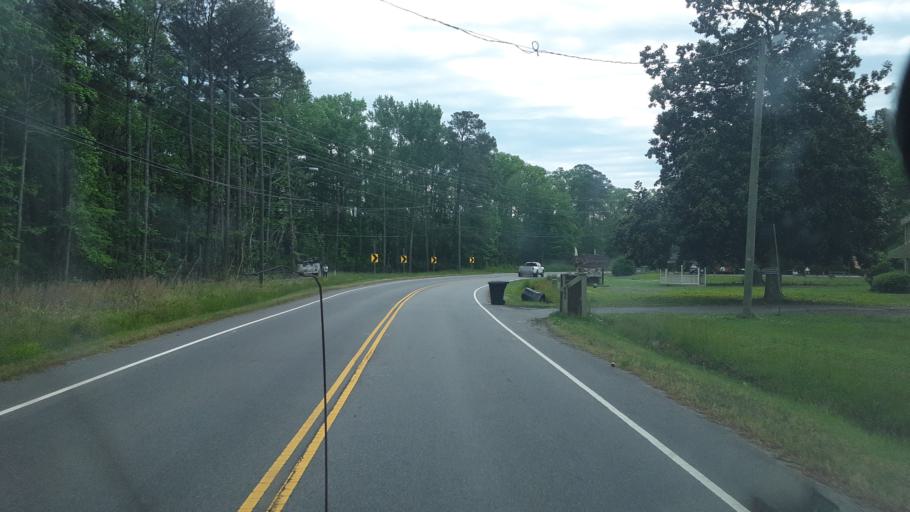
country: US
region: Virginia
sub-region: City of Virginia Beach
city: Virginia Beach
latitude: 36.7451
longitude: -75.9635
